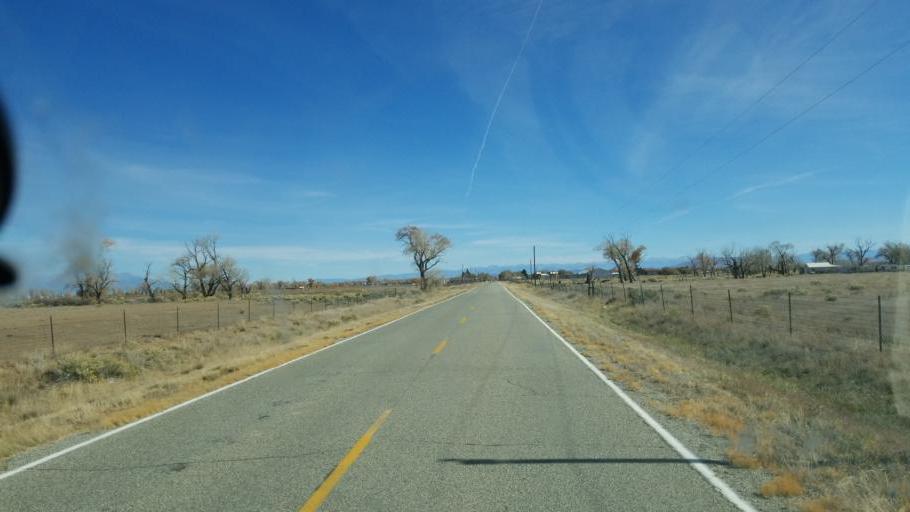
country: US
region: Colorado
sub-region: Conejos County
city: Conejos
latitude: 37.2834
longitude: -106.1213
